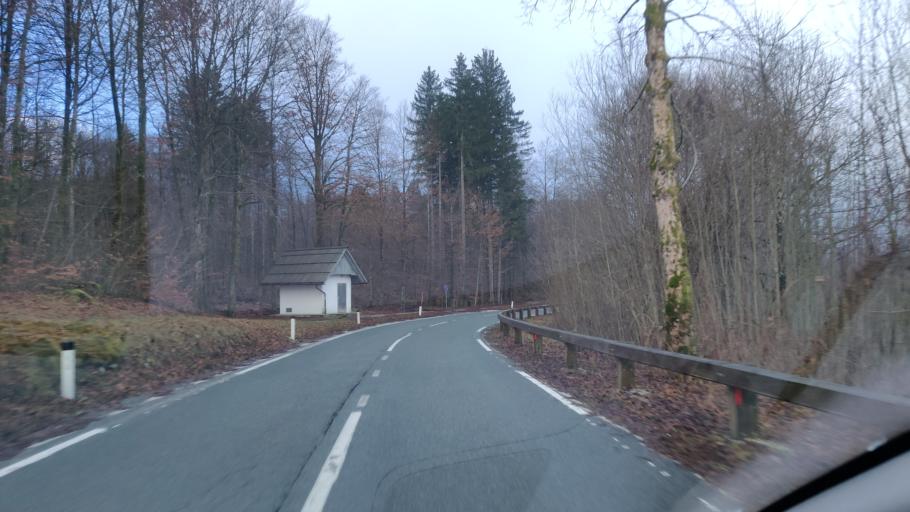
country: SI
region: Bohinj
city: Bohinjska Bistrica
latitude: 46.2806
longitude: 13.8535
